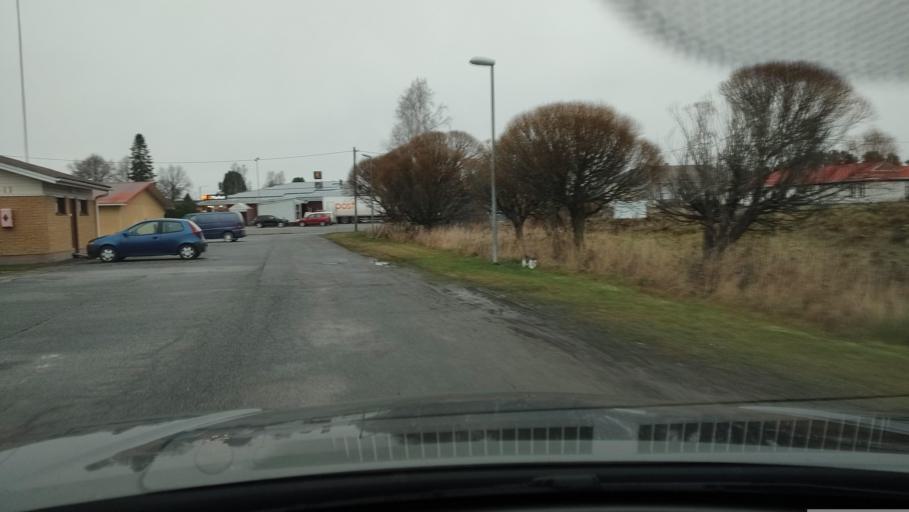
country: FI
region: Ostrobothnia
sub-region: Sydosterbotten
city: Kristinestad
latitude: 62.2534
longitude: 21.5064
